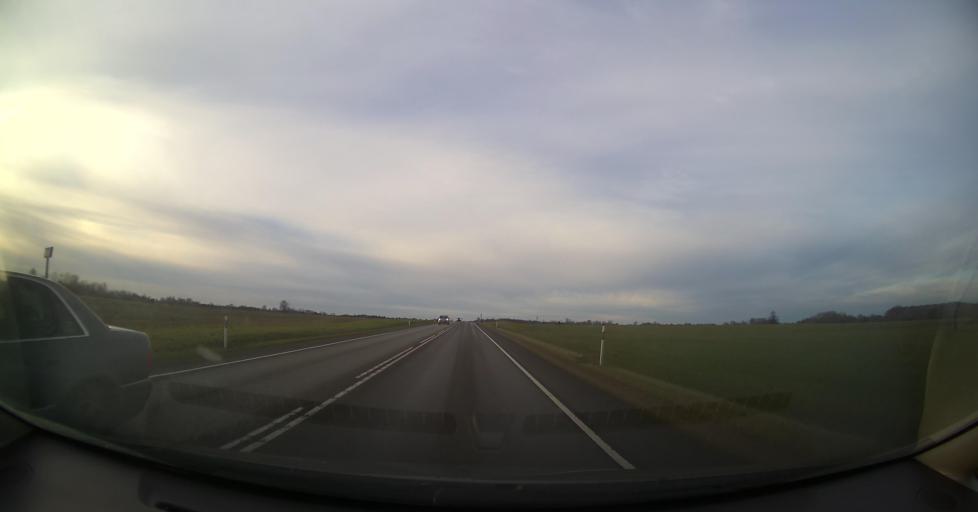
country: EE
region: Ida-Virumaa
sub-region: Sillamaee linn
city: Sillamae
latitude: 59.3838
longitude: 27.8328
